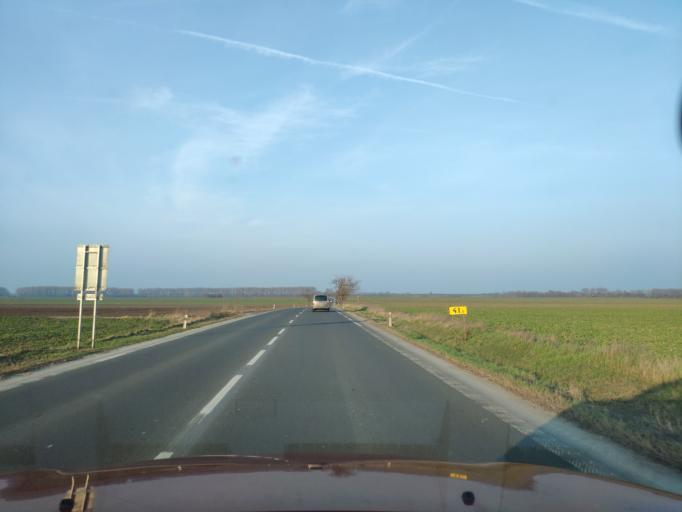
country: SK
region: Trnavsky
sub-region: Okres Trnava
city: Trnava
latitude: 48.3165
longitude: 17.5077
